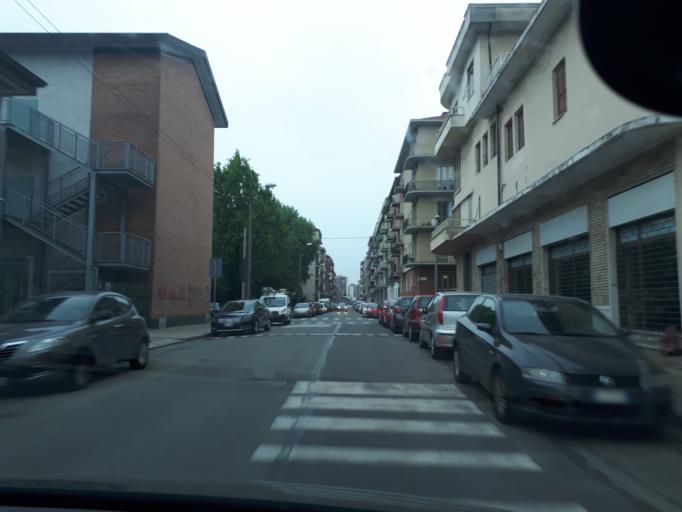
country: IT
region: Piedmont
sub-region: Provincia di Torino
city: Lesna
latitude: 45.0730
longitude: 7.6102
